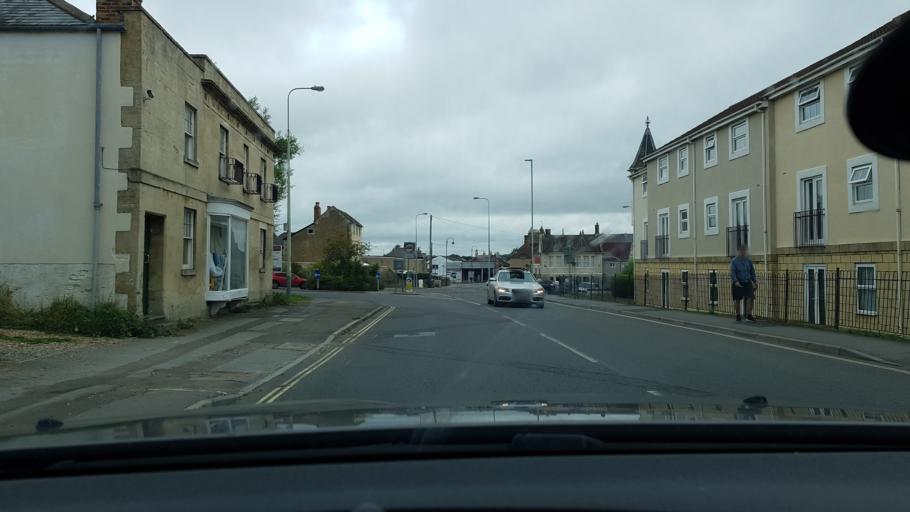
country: GB
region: England
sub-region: Wiltshire
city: Chippenham
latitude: 51.4543
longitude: -2.1098
